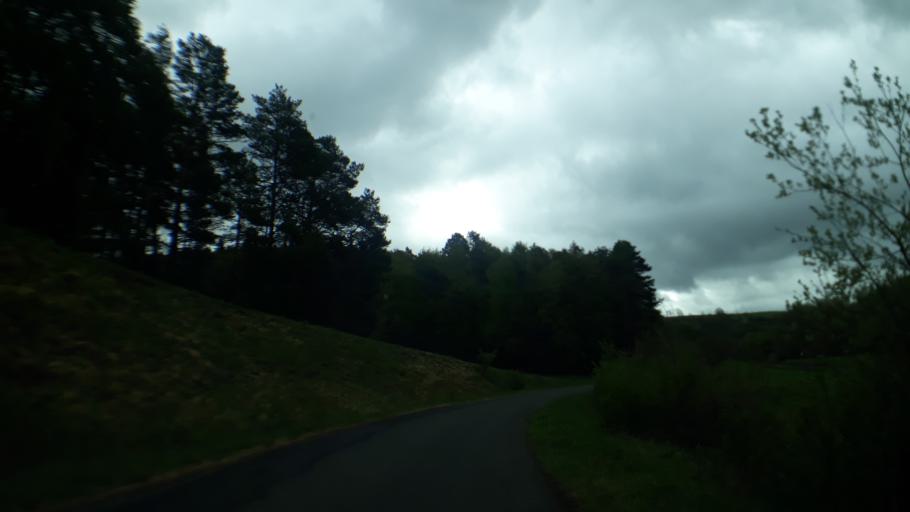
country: DE
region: North Rhine-Westphalia
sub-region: Regierungsbezirk Koln
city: Nettersheim
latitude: 50.5101
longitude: 6.6217
